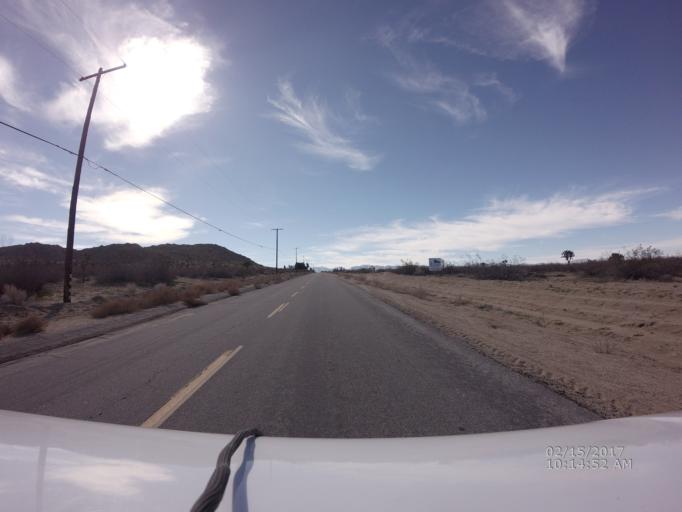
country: US
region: California
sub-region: Los Angeles County
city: Lake Los Angeles
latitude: 34.6109
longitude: -117.8715
